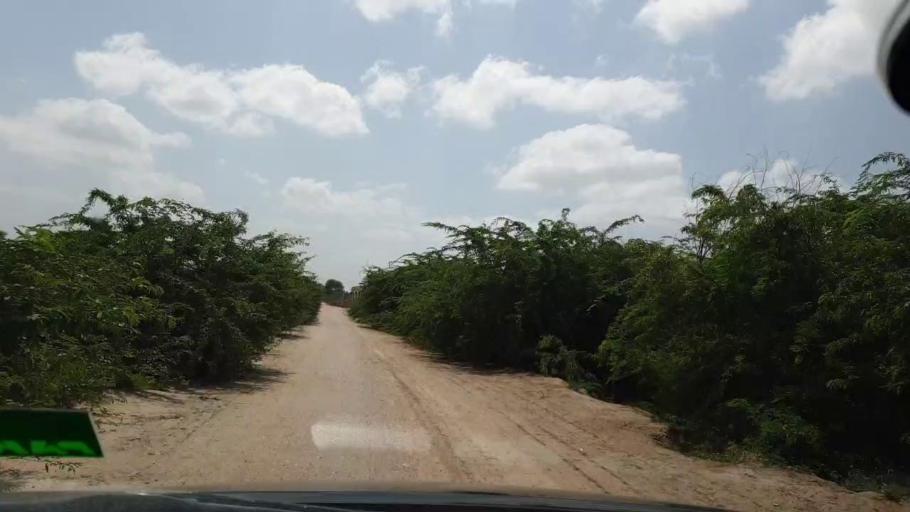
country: PK
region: Sindh
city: Kadhan
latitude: 24.5642
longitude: 69.2110
